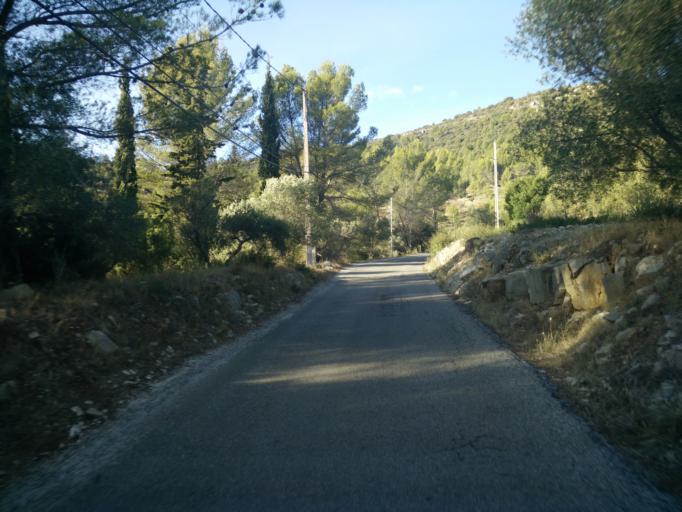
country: FR
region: Provence-Alpes-Cote d'Azur
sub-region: Departement du Var
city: Sollies-Toucas
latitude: 43.2064
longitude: 5.9947
